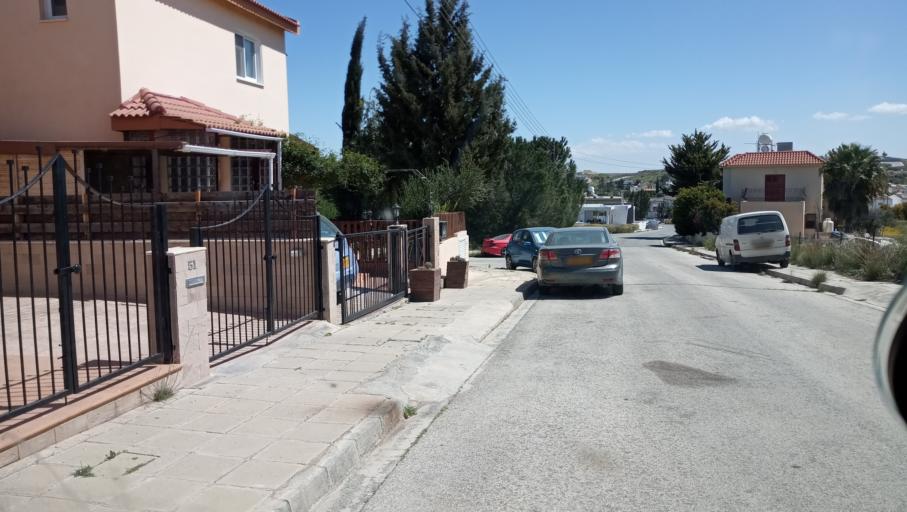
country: CY
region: Lefkosia
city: Dali
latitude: 35.0620
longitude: 33.3932
